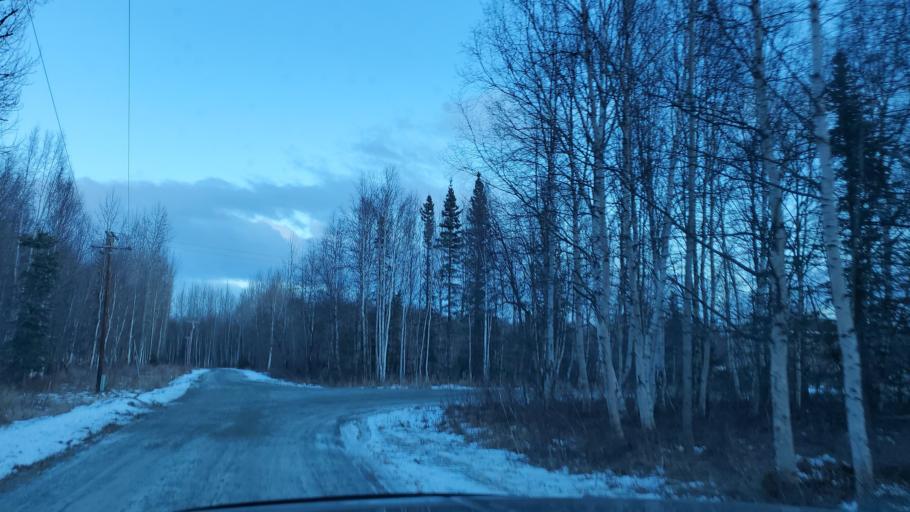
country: US
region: Alaska
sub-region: Matanuska-Susitna Borough
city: Lakes
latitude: 61.6652
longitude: -149.3372
